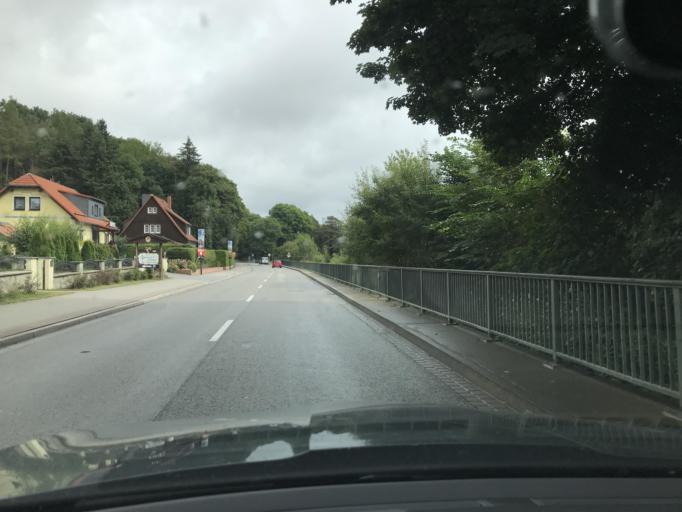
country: DE
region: Saxony-Anhalt
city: Elbingerode
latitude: 51.7689
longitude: 10.8104
